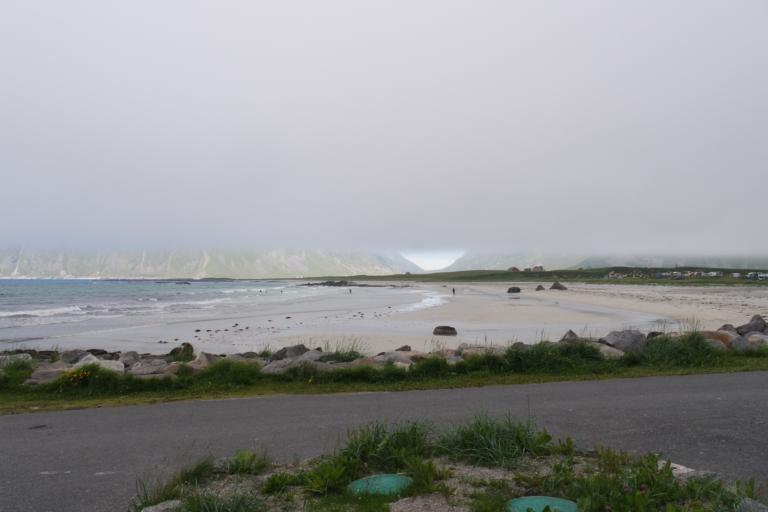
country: NO
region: Nordland
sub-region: Flakstad
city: Ramberg
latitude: 68.1038
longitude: 13.2842
